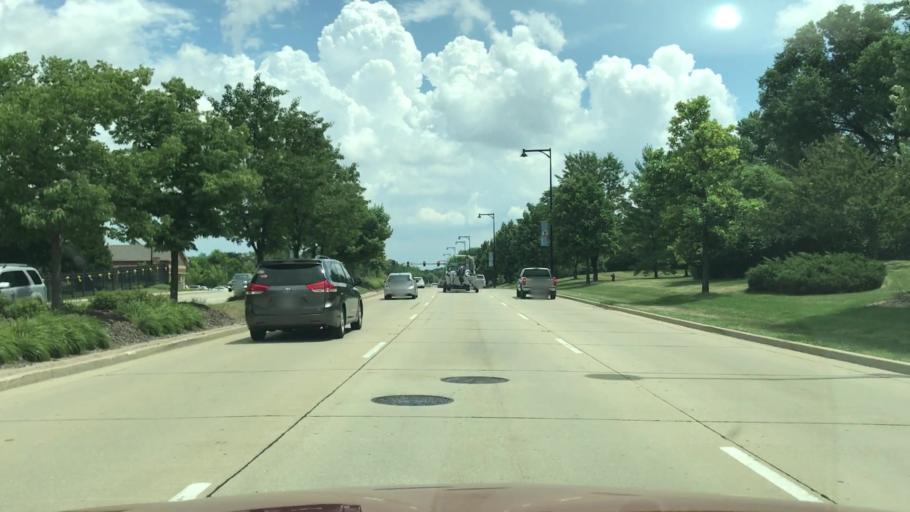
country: US
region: Illinois
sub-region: DuPage County
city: Bloomingdale
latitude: 41.9571
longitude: -88.0678
